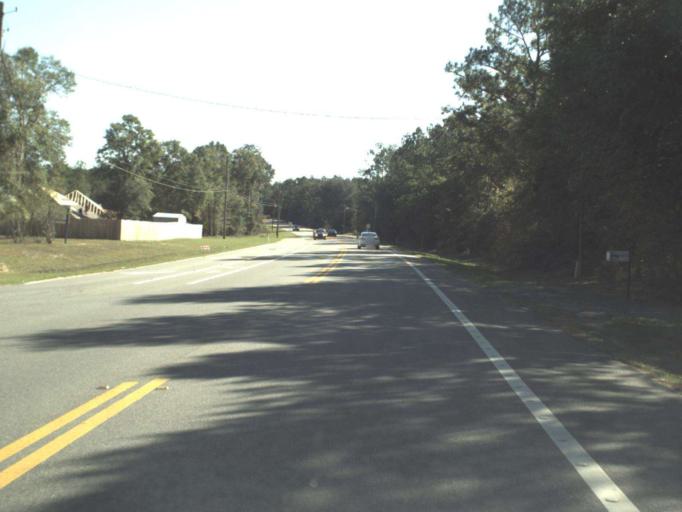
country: US
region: Florida
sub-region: Okaloosa County
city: Crestview
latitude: 30.7650
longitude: -86.6675
